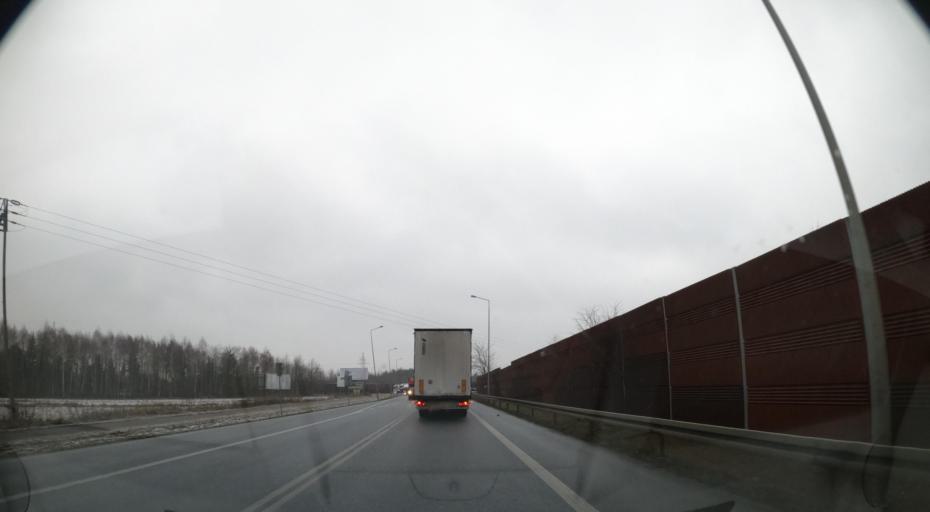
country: PL
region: Masovian Voivodeship
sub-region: Powiat sochaczewski
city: Sochaczew
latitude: 52.2182
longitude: 20.2060
